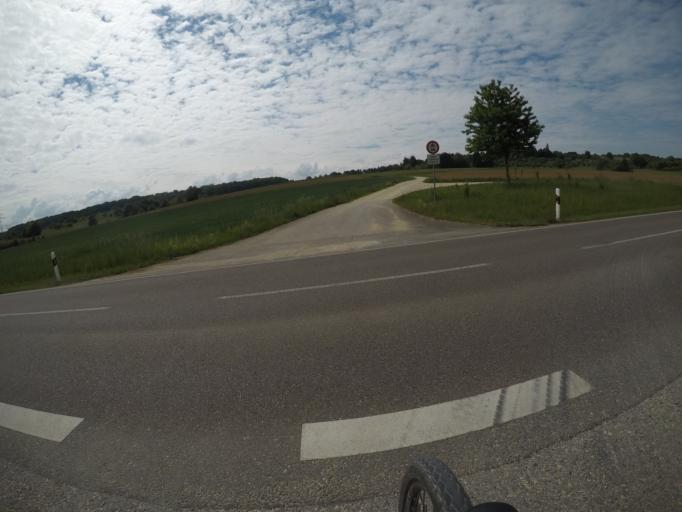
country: DE
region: Baden-Wuerttemberg
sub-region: Regierungsbezirk Stuttgart
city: Notzingen
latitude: 48.6695
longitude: 9.4414
